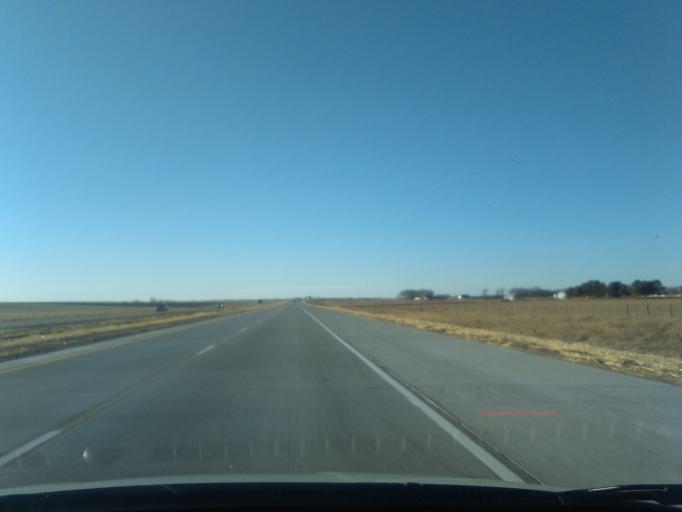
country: US
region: Nebraska
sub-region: Deuel County
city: Chappell
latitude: 41.0872
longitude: -102.4990
